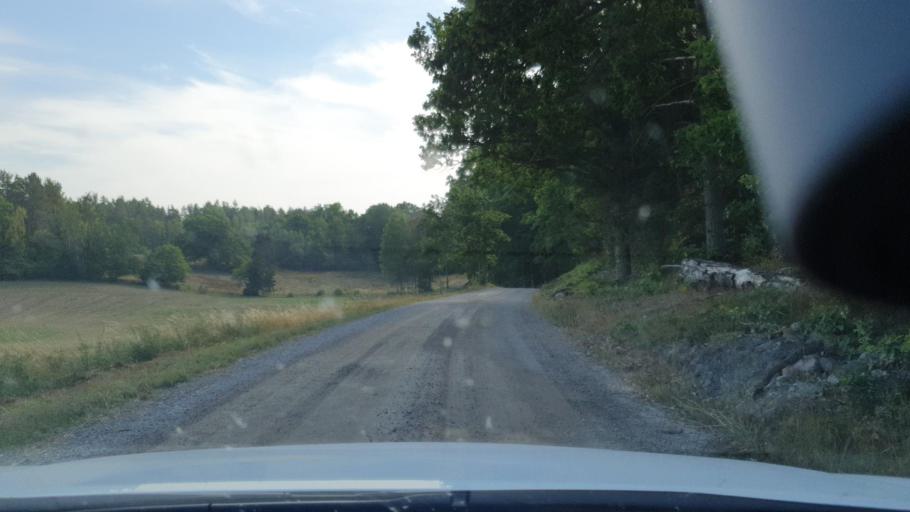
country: SE
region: Kalmar
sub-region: Vasterviks Kommun
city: Ankarsrum
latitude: 57.7025
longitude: 16.4544
